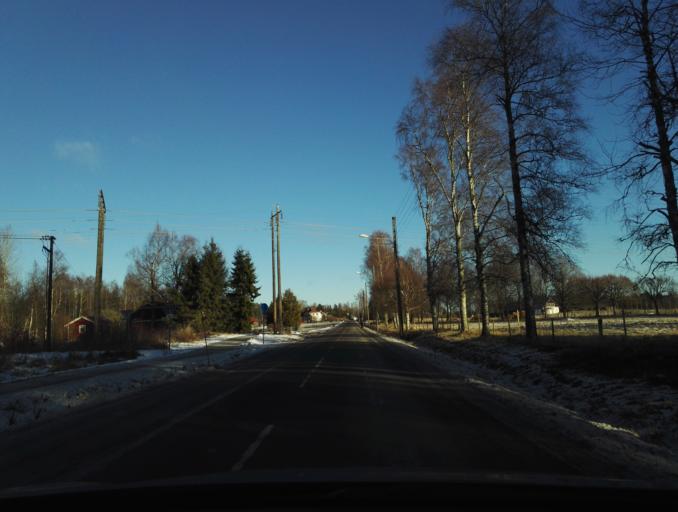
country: SE
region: Kronoberg
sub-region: Vaxjo Kommun
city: Gemla
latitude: 56.8587
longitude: 14.6277
